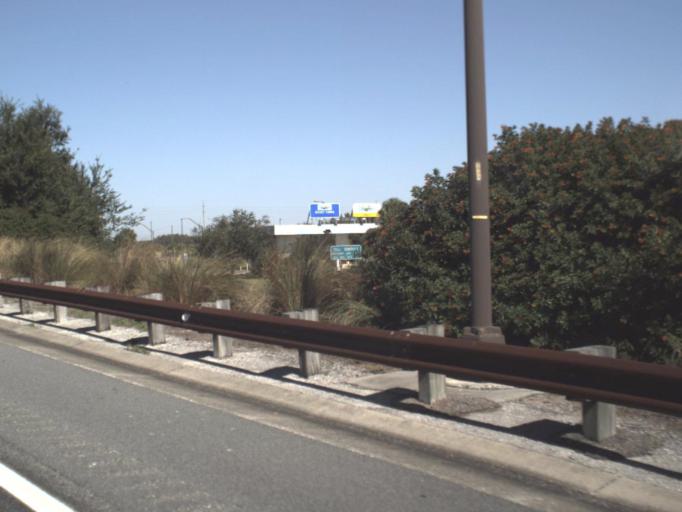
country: US
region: Florida
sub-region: Hillsborough County
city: Cheval
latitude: 28.1871
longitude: -82.5420
